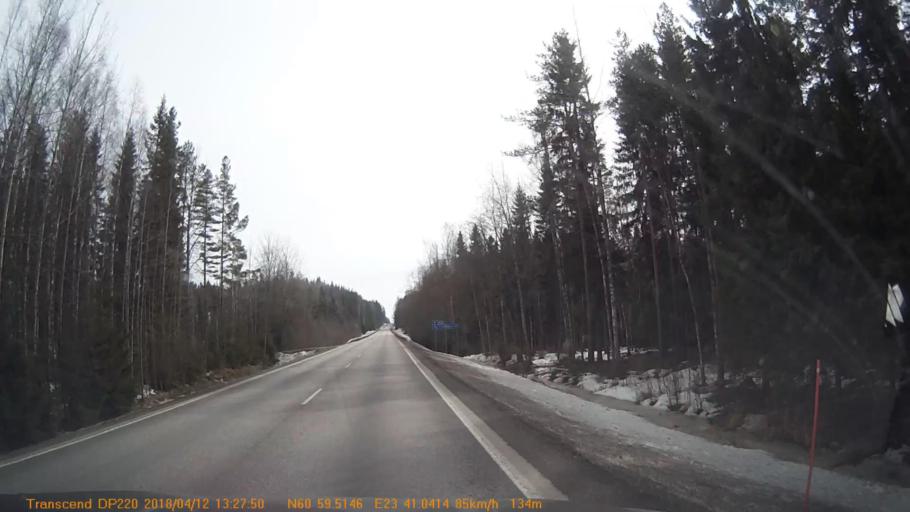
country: FI
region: Pirkanmaa
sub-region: Etelae-Pirkanmaa
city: Kylmaekoski
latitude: 60.9918
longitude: 23.6841
